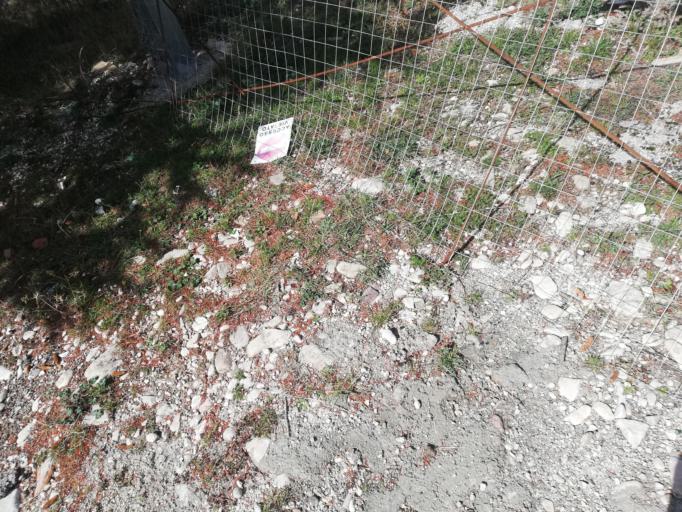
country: IT
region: Apulia
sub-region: Provincia di Foggia
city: Biccari
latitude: 41.3689
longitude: 15.1720
